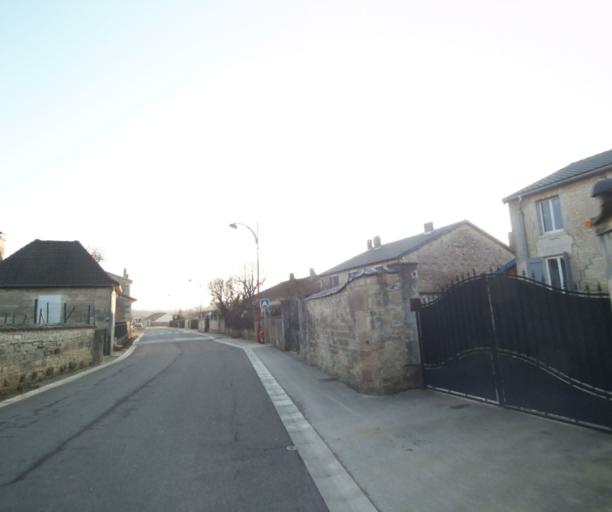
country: FR
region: Champagne-Ardenne
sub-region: Departement de la Haute-Marne
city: Chevillon
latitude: 48.5435
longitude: 5.1019
